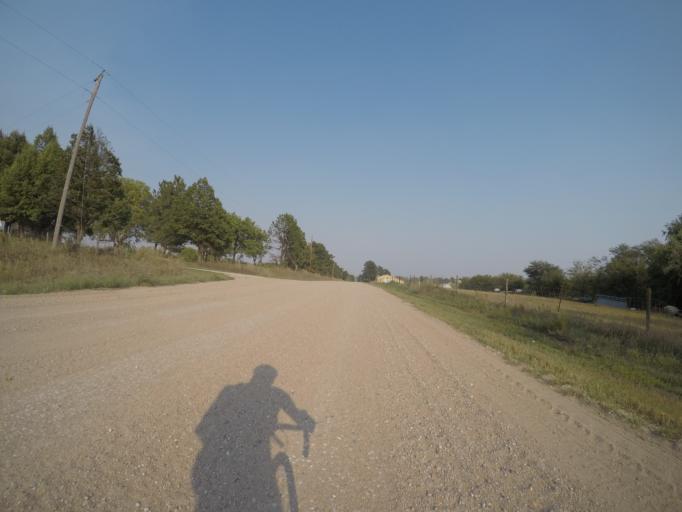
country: US
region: Nebraska
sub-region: Gage County
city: Beatrice
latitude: 40.2629
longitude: -96.8018
